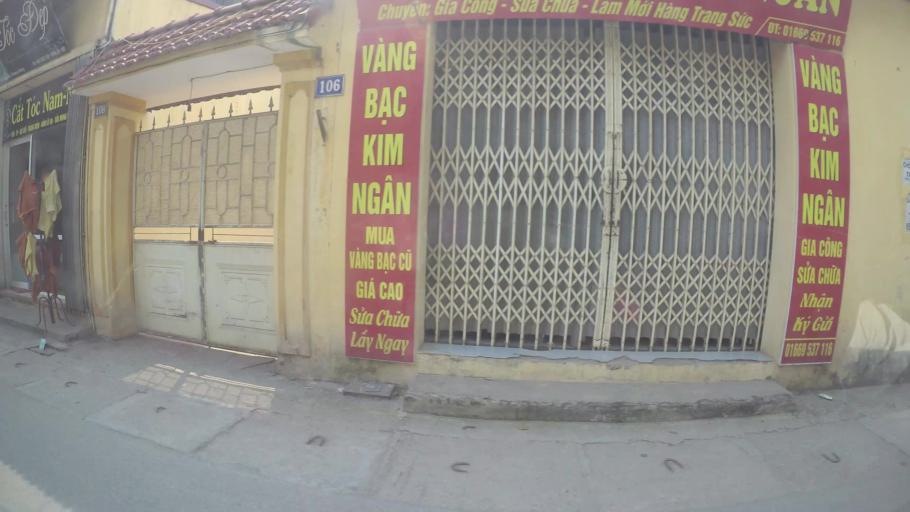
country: VN
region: Ha Noi
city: Ha Dong
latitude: 20.9981
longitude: 105.7565
